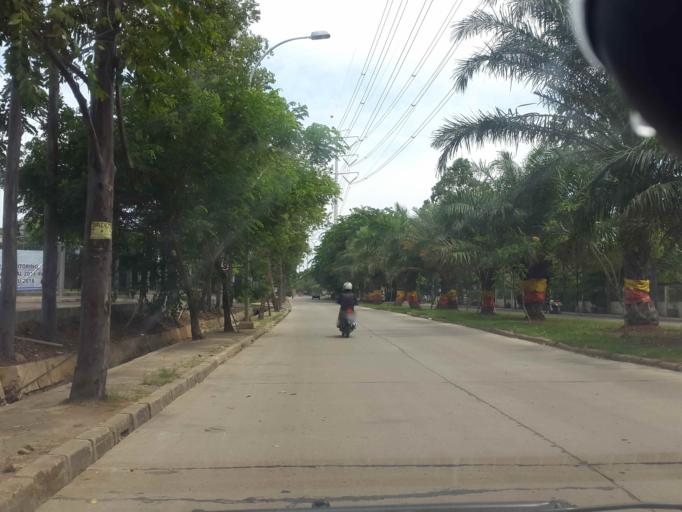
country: ID
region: Banten
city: Tangerang
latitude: -6.1546
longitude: 106.6432
